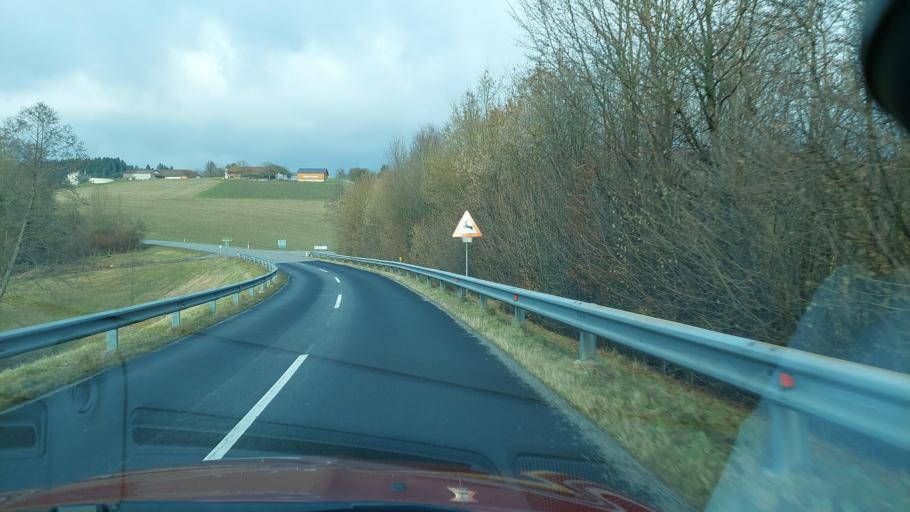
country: AT
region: Upper Austria
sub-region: Politischer Bezirk Grieskirchen
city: Grieskirchen
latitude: 48.1976
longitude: 13.8412
